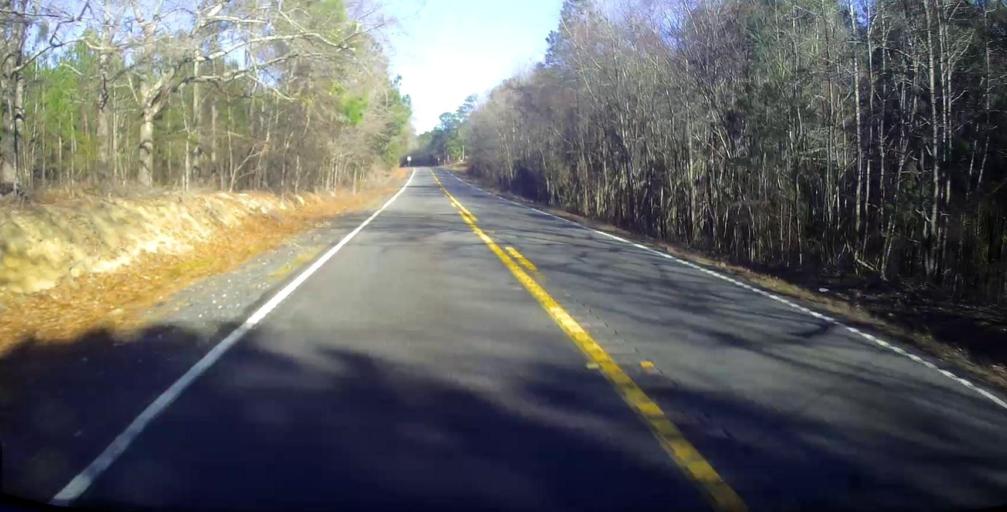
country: US
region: Georgia
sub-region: Talbot County
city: Talbotton
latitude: 32.6462
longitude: -84.3775
